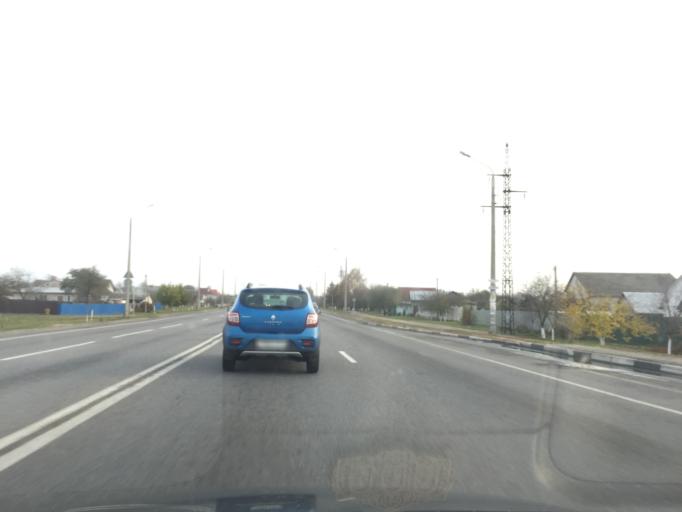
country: BY
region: Gomel
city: Gomel
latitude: 52.4937
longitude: 30.9610
